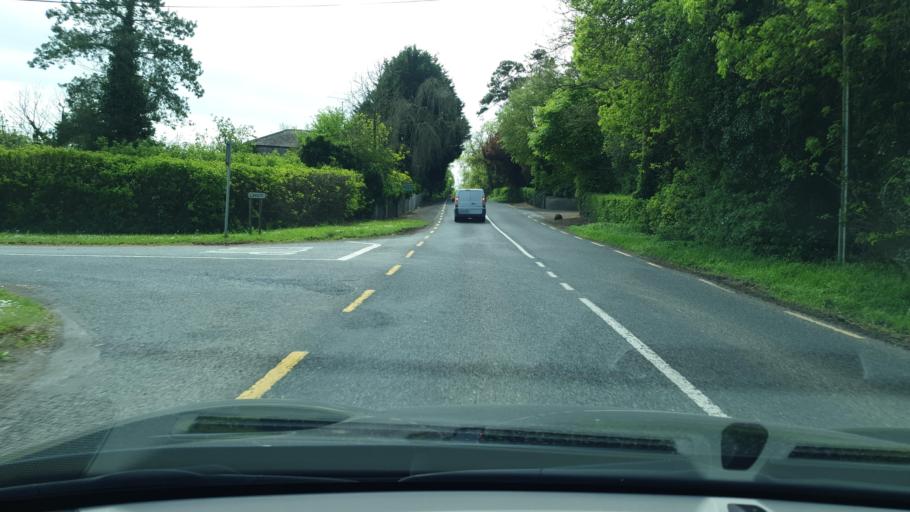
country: IE
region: Leinster
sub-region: An Mhi
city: Navan
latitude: 53.7491
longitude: -6.7189
